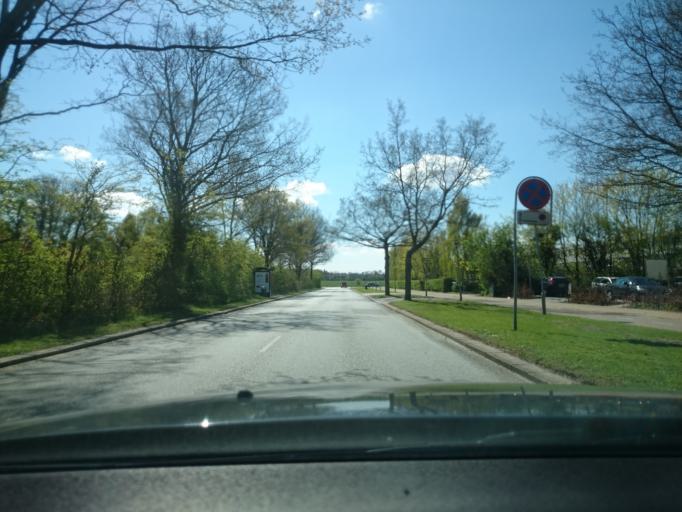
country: DK
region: Capital Region
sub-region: Lyngby-Tarbaek Kommune
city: Kongens Lyngby
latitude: 55.7892
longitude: 12.5338
